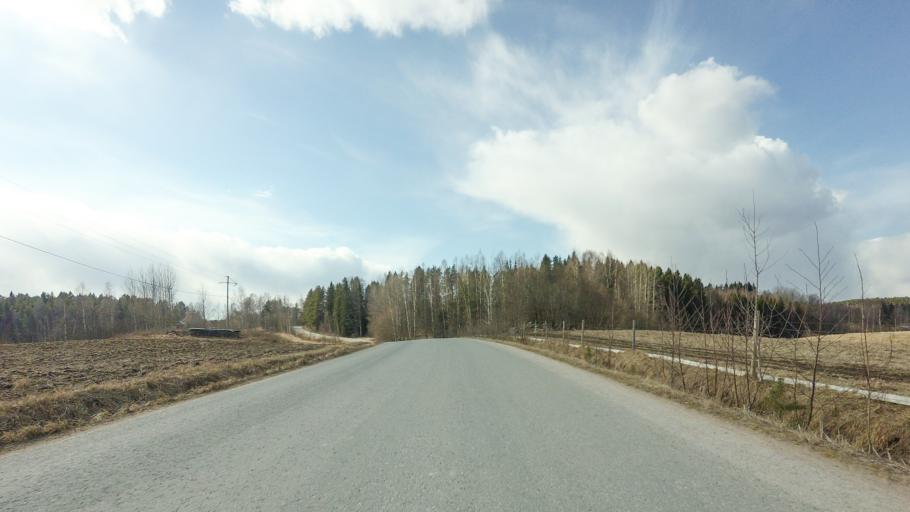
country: FI
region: Varsinais-Suomi
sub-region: Salo
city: Suomusjaervi
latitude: 60.3460
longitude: 23.6958
